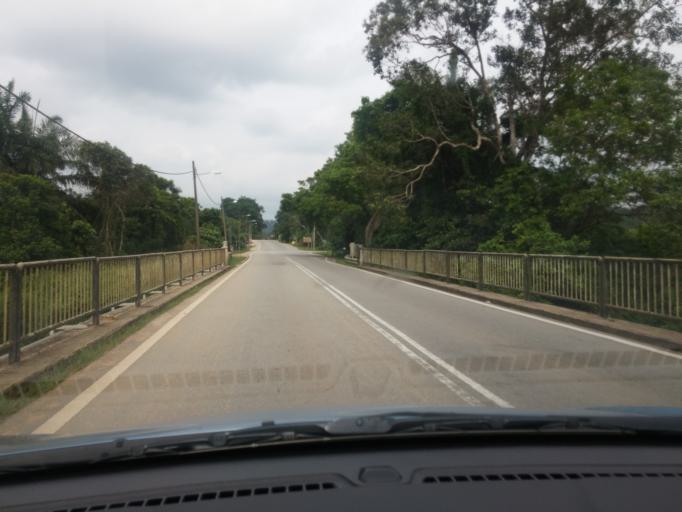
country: MY
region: Pahang
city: Kuantan
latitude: 3.8808
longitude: 103.1733
